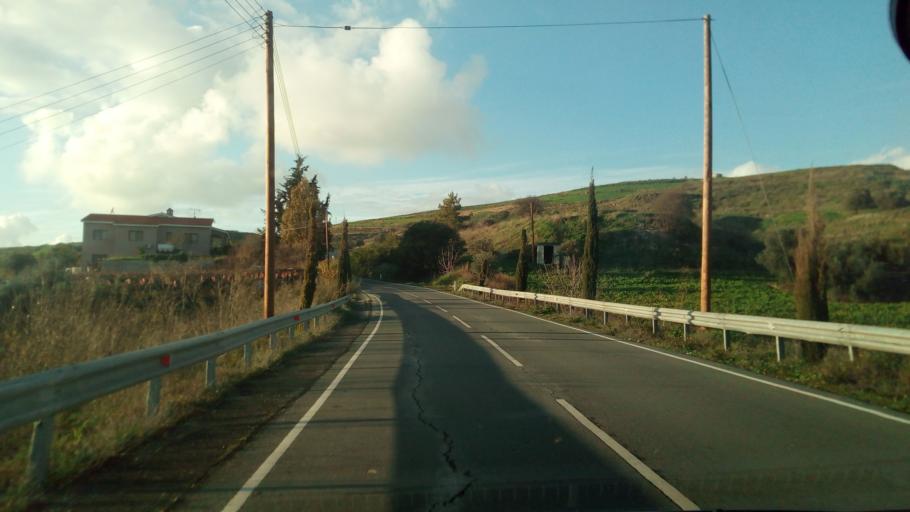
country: CY
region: Pafos
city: Mesogi
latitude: 34.9126
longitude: 32.5467
